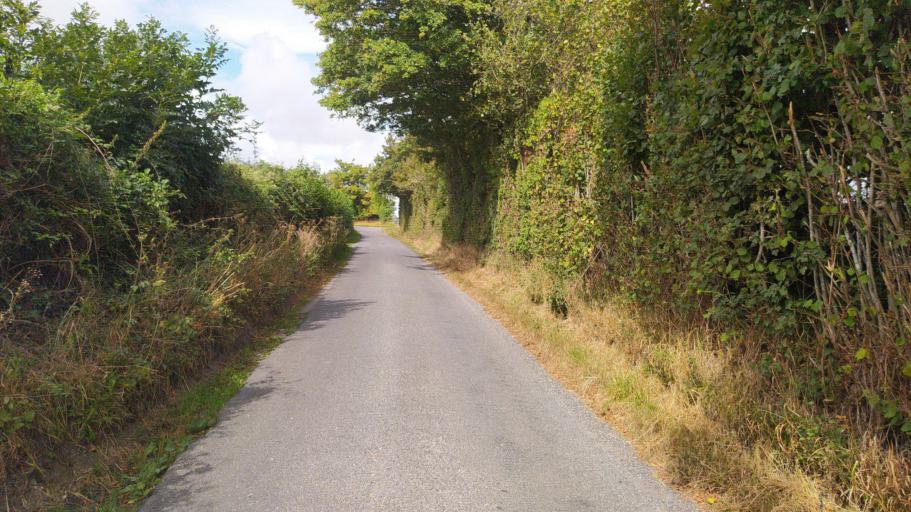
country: GB
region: England
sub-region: Hampshire
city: Petersfield
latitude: 50.9906
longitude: -0.9972
